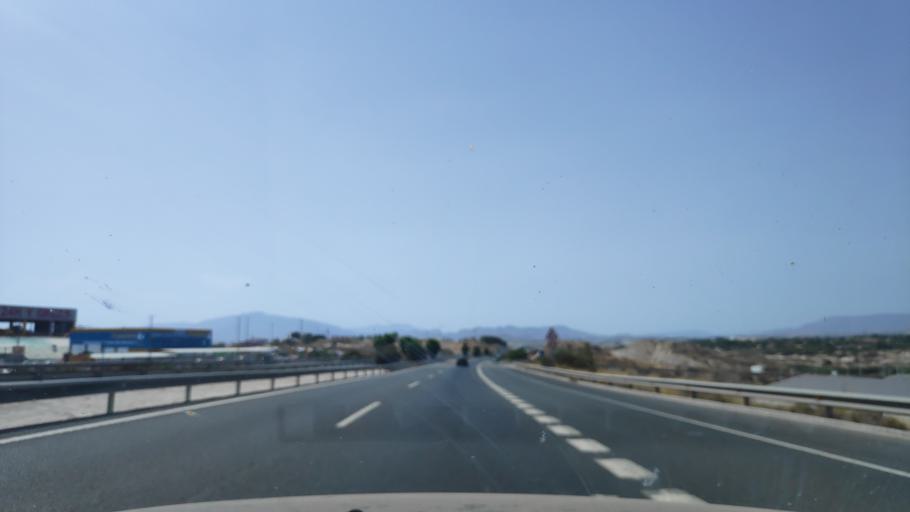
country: ES
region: Murcia
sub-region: Murcia
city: Molina de Segura
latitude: 38.0708
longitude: -1.2000
